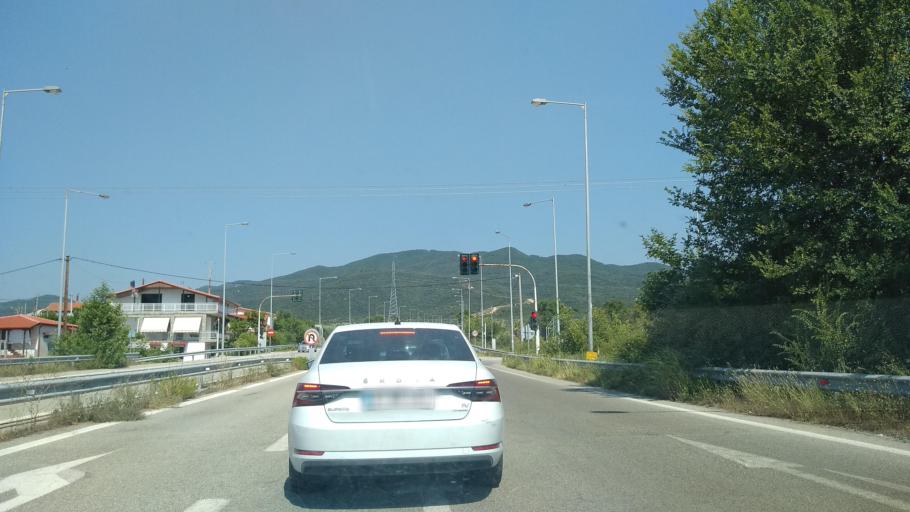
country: GR
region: Central Macedonia
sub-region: Nomos Thessalonikis
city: Nea Vrasna
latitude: 40.7055
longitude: 23.6908
